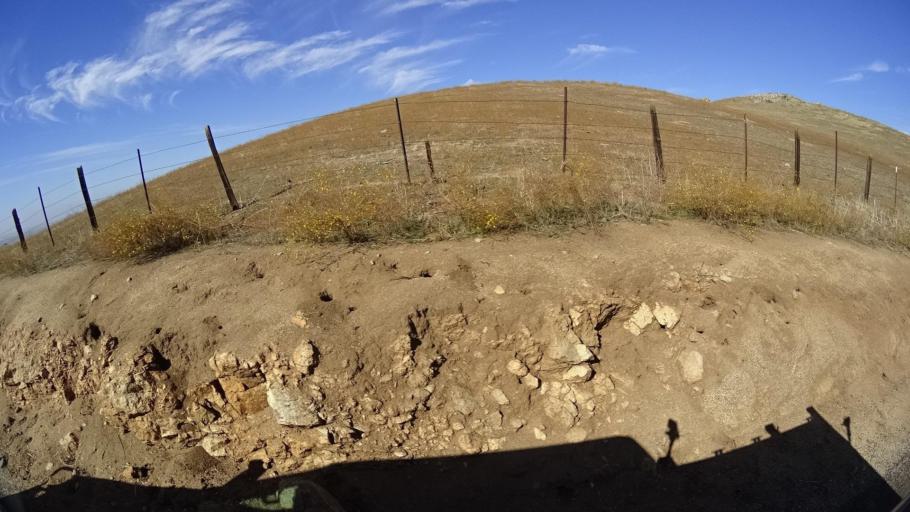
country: US
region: California
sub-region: Tulare County
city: Richgrove
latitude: 35.6899
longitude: -118.8750
